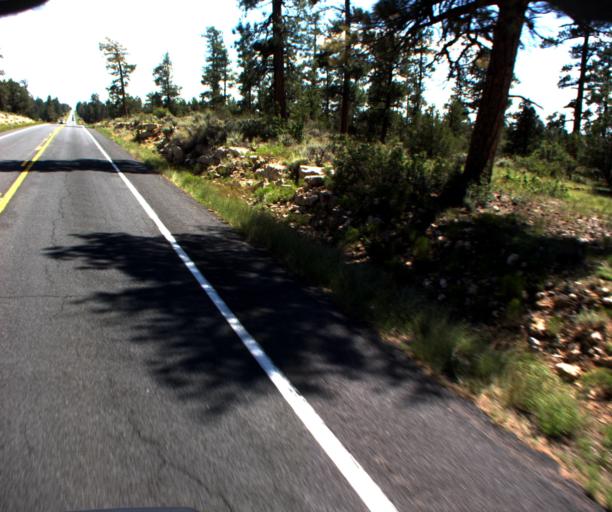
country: US
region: Arizona
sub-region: Coconino County
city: Grand Canyon Village
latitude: 35.9306
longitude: -112.1306
